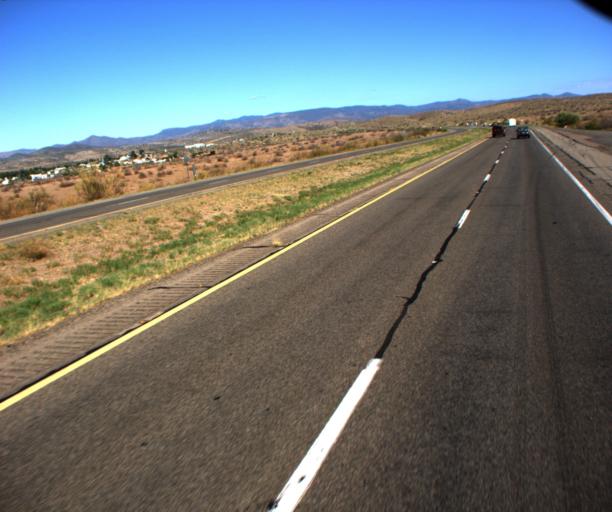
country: US
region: Arizona
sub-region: Yavapai County
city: Spring Valley
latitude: 34.3427
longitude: -112.1385
